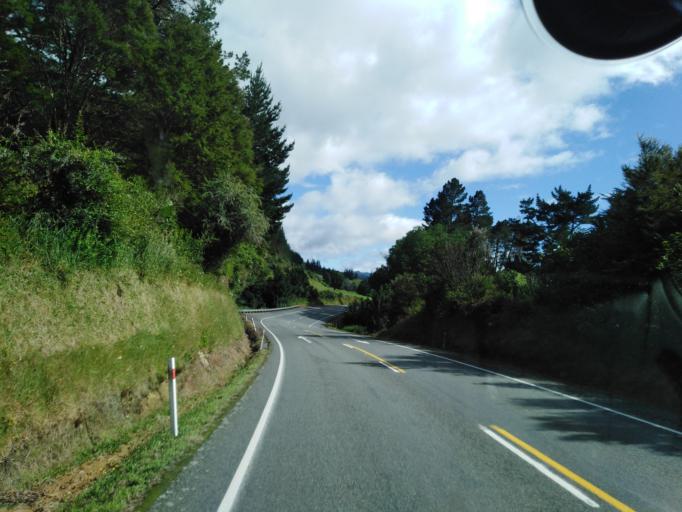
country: NZ
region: Nelson
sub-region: Nelson City
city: Nelson
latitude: -41.2860
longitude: 173.5721
